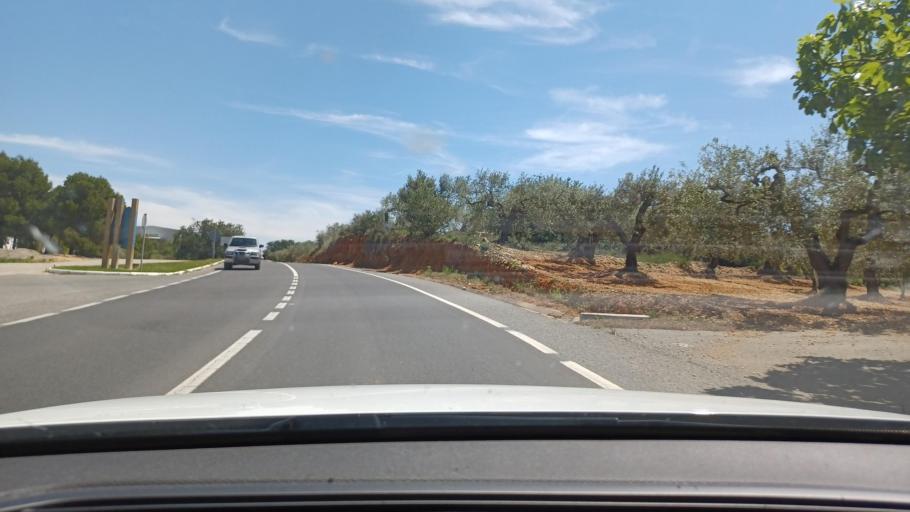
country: ES
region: Catalonia
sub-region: Provincia de Tarragona
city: Masdenverge
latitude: 40.7118
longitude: 0.5346
